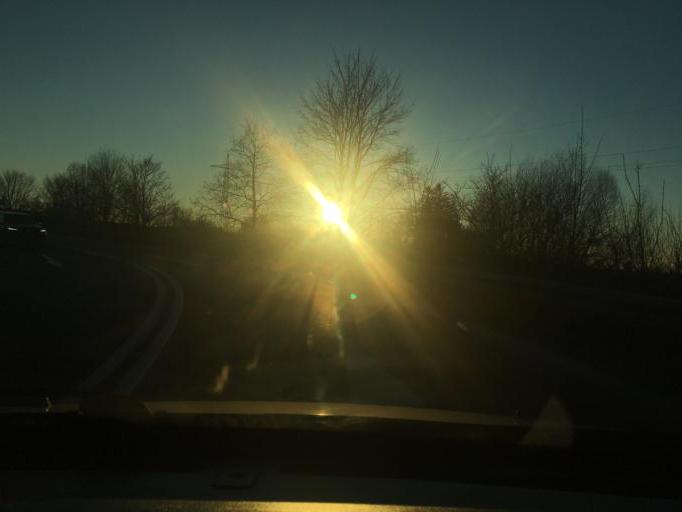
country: DE
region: Bavaria
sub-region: Swabia
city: Trunkelsberg
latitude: 47.9995
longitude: 10.2013
